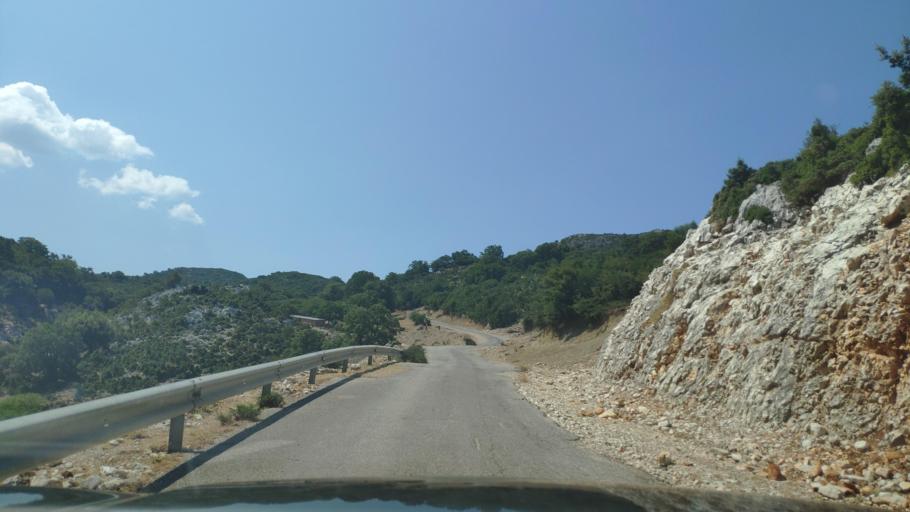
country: GR
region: West Greece
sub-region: Nomos Aitolias kai Akarnanias
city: Monastirakion
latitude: 38.8282
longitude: 20.9280
